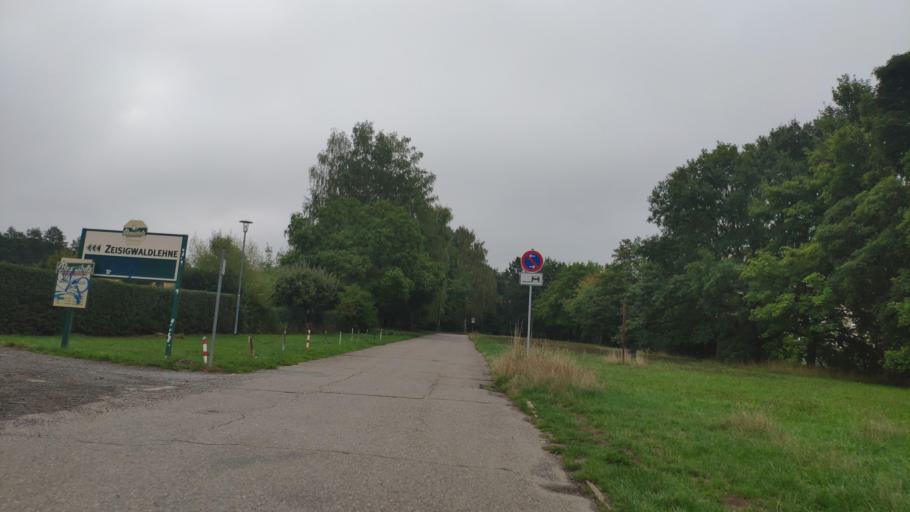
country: DE
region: Saxony
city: Hilbersdorf
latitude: 50.8346
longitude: 12.9694
